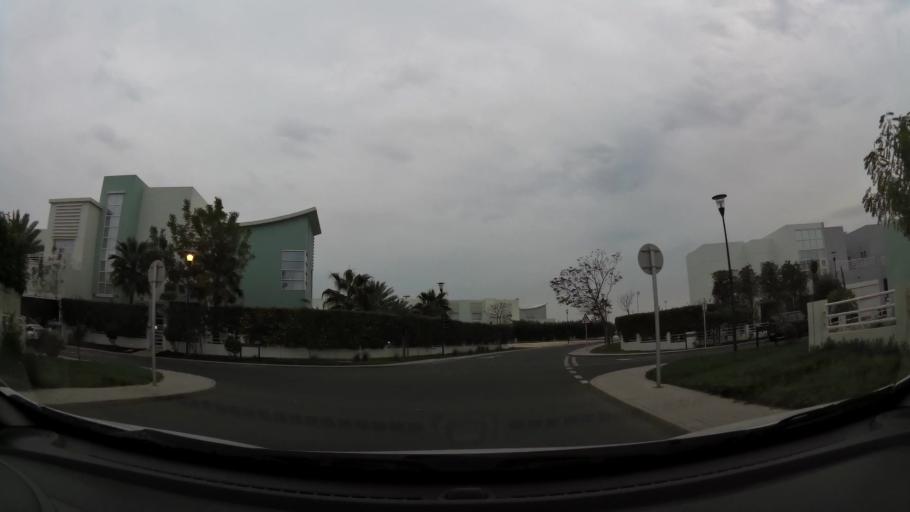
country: BH
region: Northern
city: Ar Rifa'
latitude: 26.1001
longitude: 50.5632
